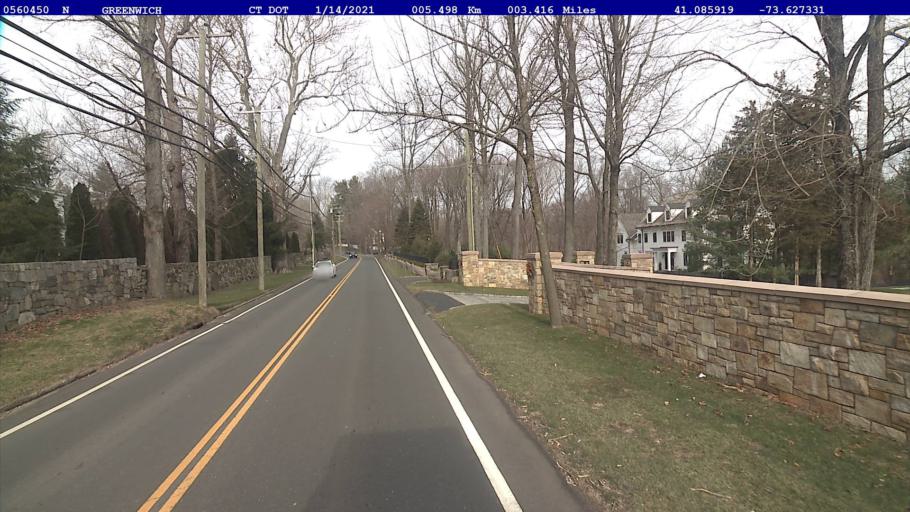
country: US
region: Connecticut
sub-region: Fairfield County
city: Cos Cob
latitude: 41.0859
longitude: -73.6273
